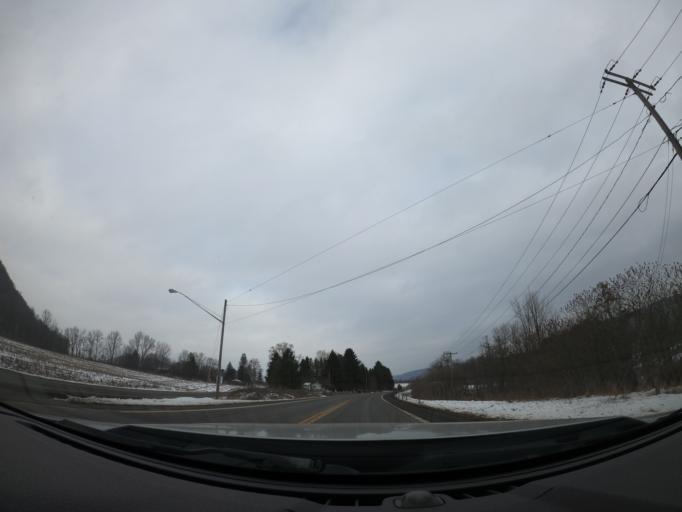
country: US
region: New York
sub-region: Cortland County
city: Homer
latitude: 42.7160
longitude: -76.1541
